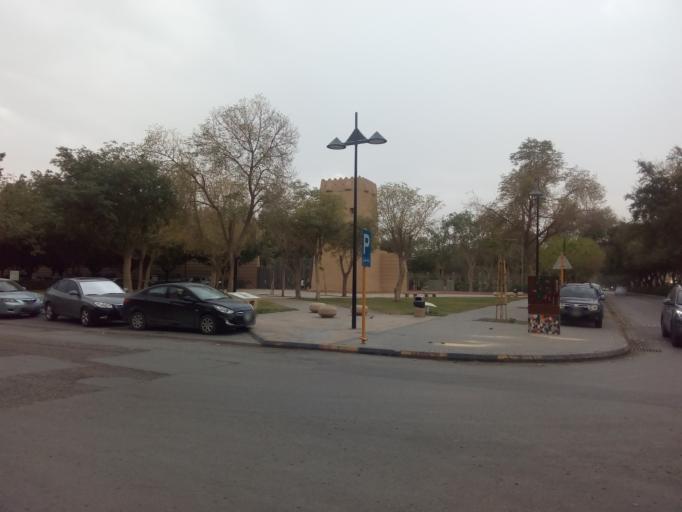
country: SA
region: Ar Riyad
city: Riyadh
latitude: 24.6494
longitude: 46.7066
